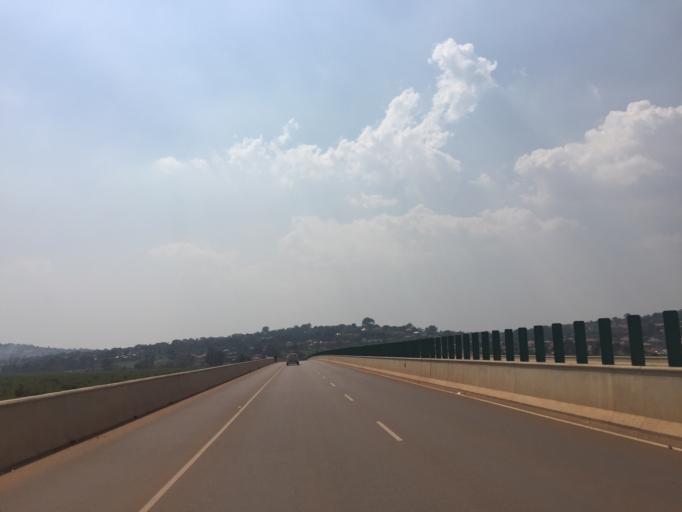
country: UG
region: Central Region
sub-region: Kampala District
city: Kampala
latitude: 0.2376
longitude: 32.6145
